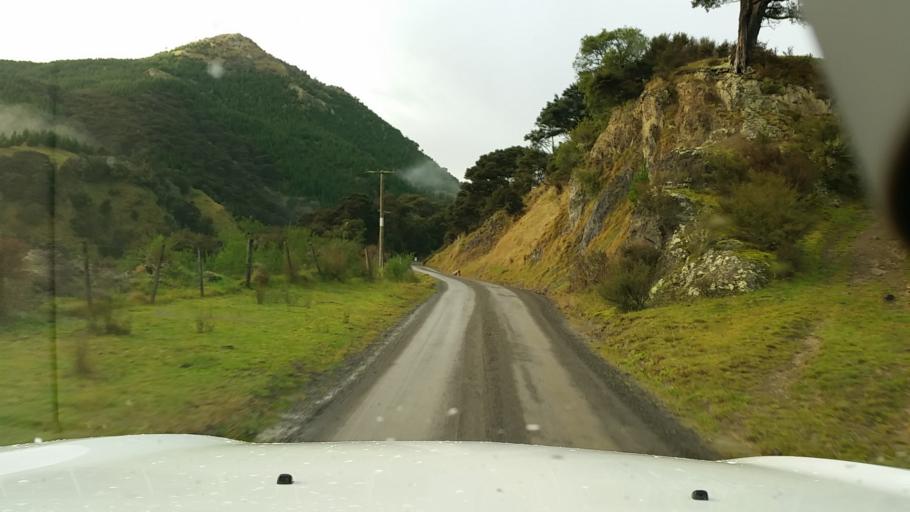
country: NZ
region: Wellington
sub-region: South Wairarapa District
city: Waipawa
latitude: -41.3398
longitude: 175.6685
